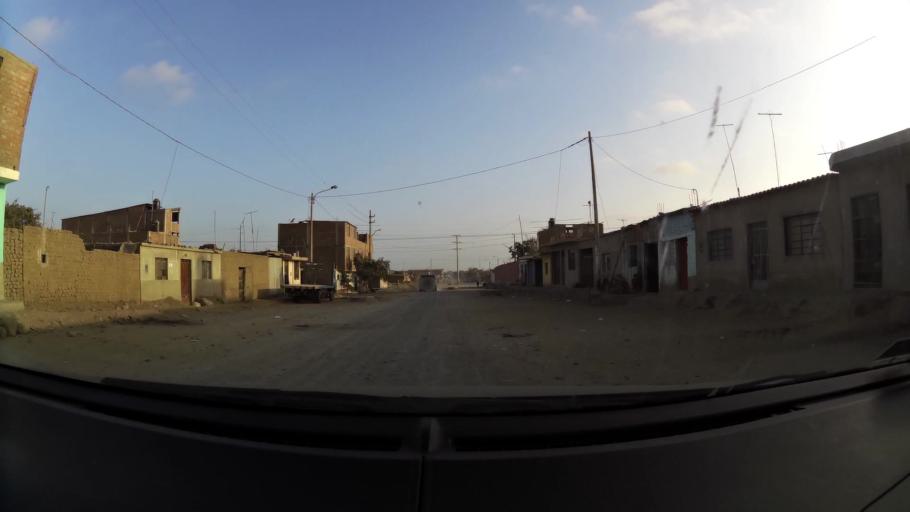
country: PE
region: La Libertad
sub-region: Provincia de Trujillo
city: El Porvenir
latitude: -8.0648
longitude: -78.9950
